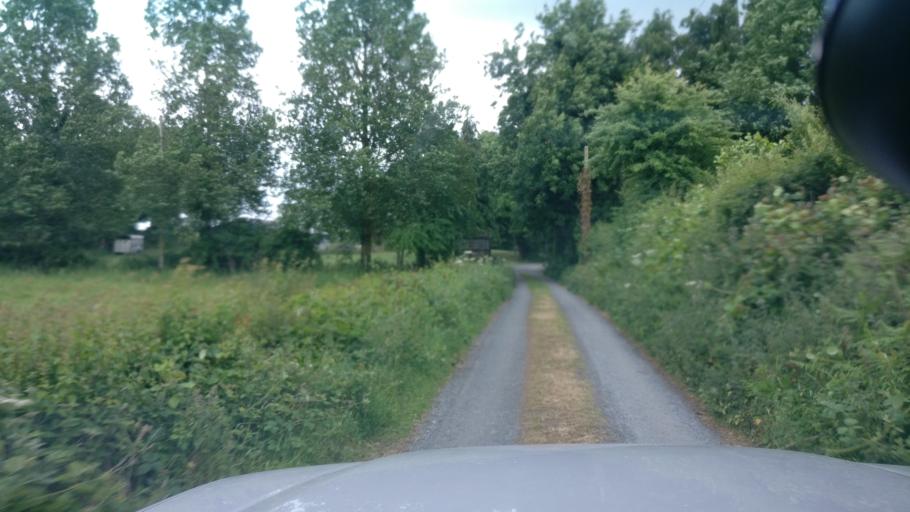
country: IE
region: Connaught
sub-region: County Galway
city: Ballinasloe
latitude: 53.2996
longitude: -8.2872
